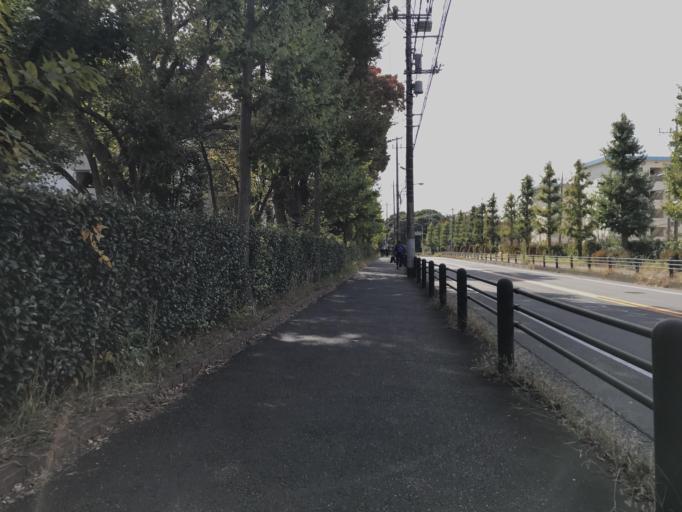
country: JP
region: Saitama
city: Wako
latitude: 35.7806
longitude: 139.6052
